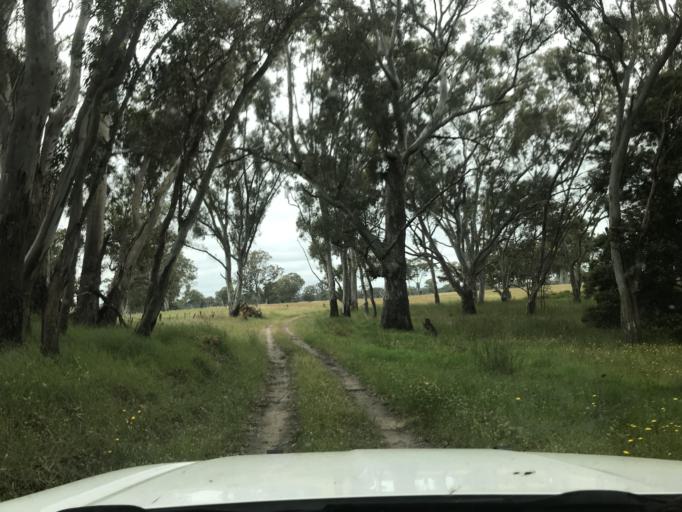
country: AU
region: South Australia
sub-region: Wattle Range
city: Penola
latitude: -37.1927
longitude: 140.9720
